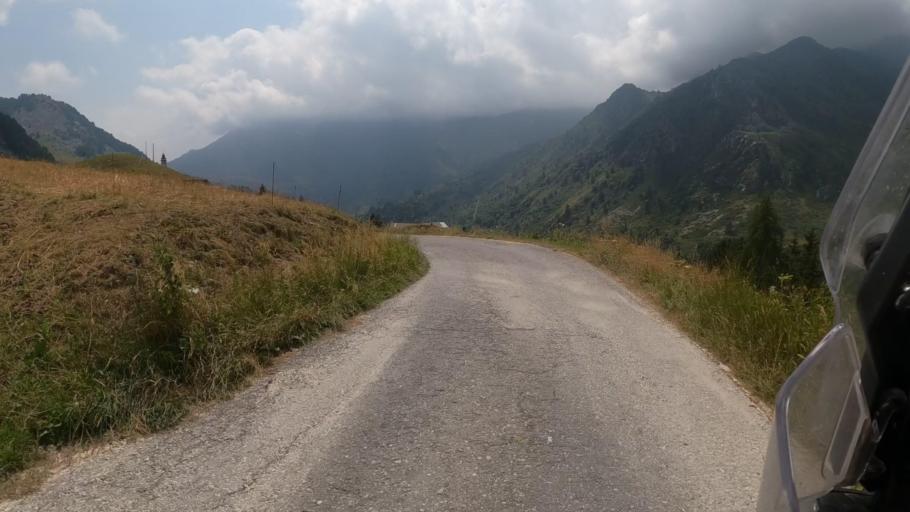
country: IT
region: Piedmont
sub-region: Provincia di Cuneo
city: Campomolino
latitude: 44.4008
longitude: 7.1667
